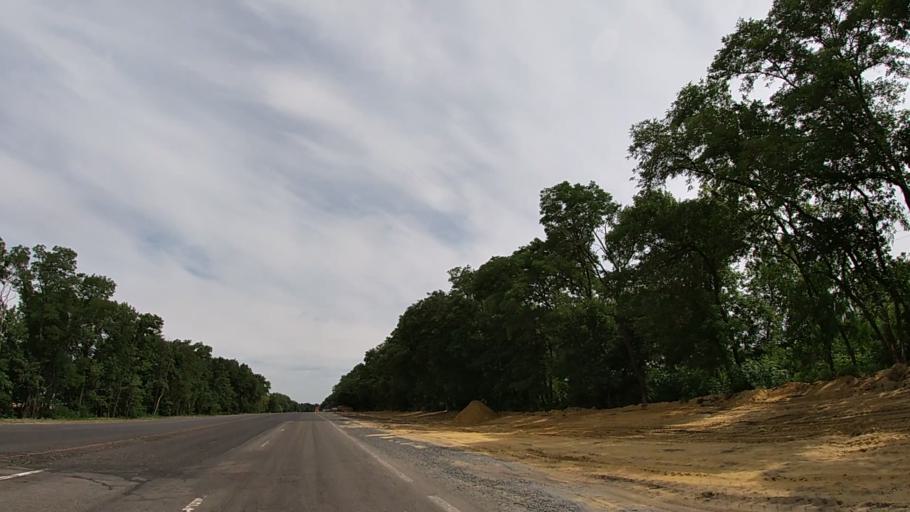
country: RU
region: Belgorod
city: Mayskiy
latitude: 50.4757
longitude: 36.4055
